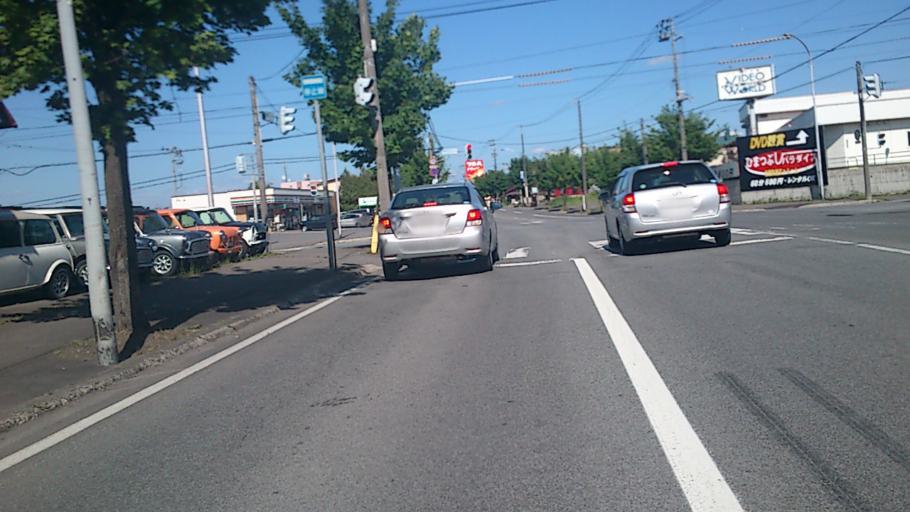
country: JP
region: Hokkaido
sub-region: Asahikawa-shi
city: Asahikawa
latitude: 43.7702
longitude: 142.4003
